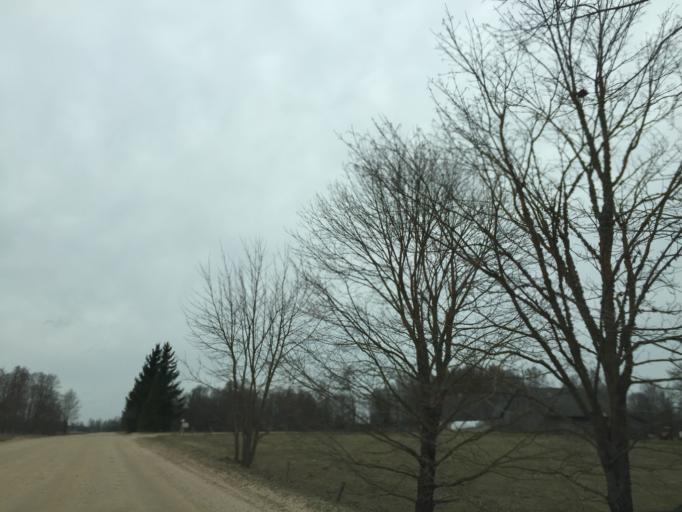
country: LV
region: Livani
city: Livani
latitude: 56.2982
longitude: 26.1722
